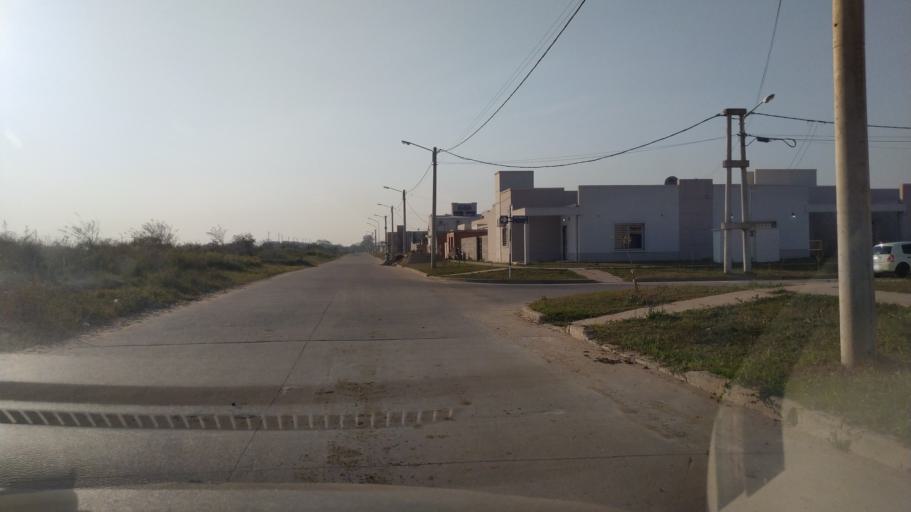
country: AR
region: Corrientes
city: Corrientes
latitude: -27.5221
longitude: -58.8067
